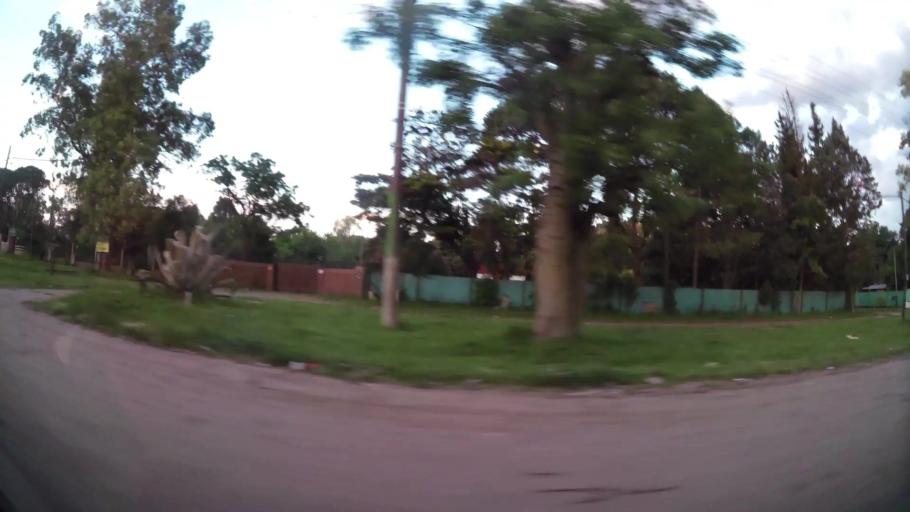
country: AR
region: Buenos Aires
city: Santa Catalina - Dique Lujan
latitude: -34.4809
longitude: -58.7791
